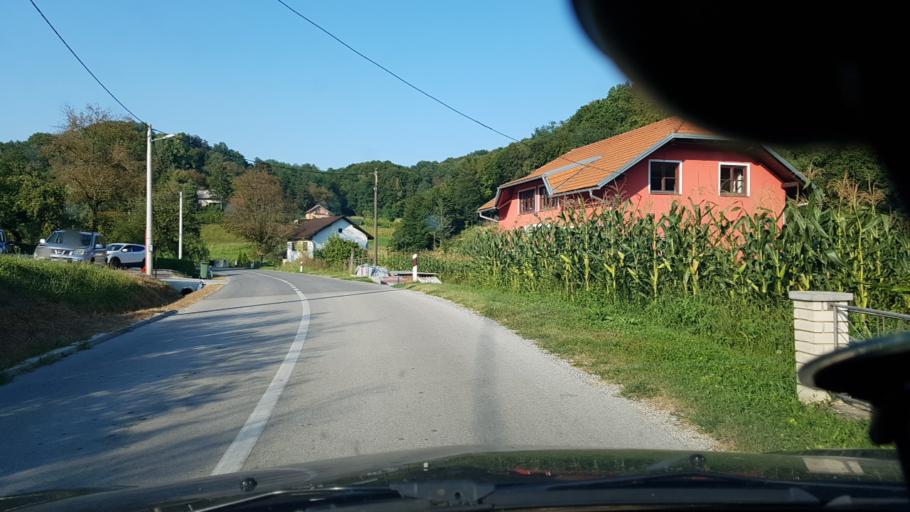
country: SI
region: Bistrica ob Sotli
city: Bistrica ob Sotli
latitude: 46.0521
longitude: 15.7703
